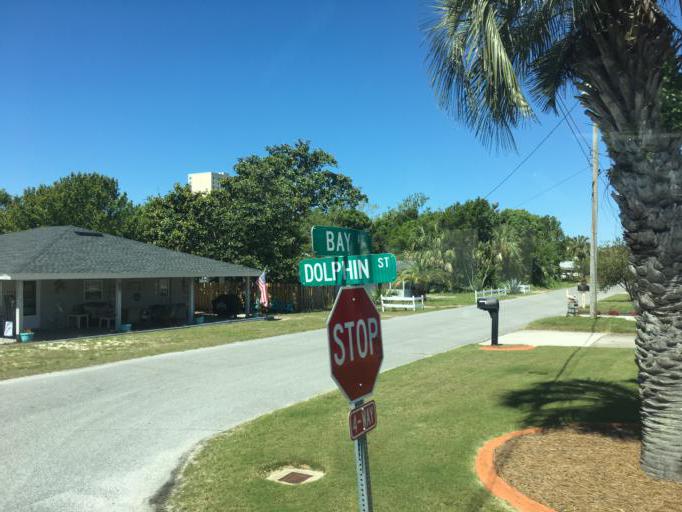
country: US
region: Florida
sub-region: Bay County
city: Panama City Beach
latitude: 30.2044
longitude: -85.8510
